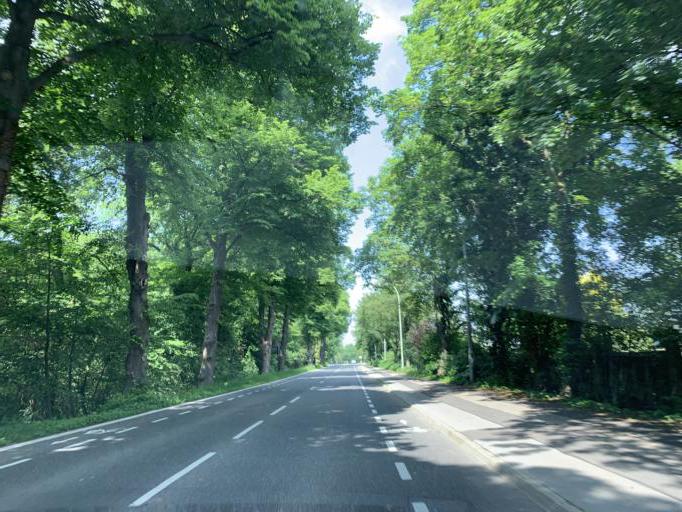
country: DE
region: North Rhine-Westphalia
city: Bruhl
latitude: 50.8037
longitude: 6.8769
